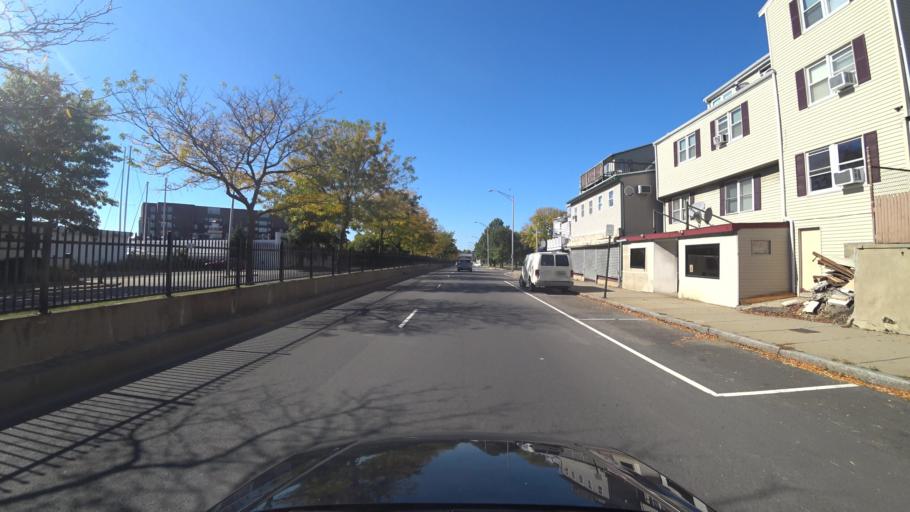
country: US
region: Massachusetts
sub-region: Essex County
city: Lynn
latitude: 42.4584
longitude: -70.9394
